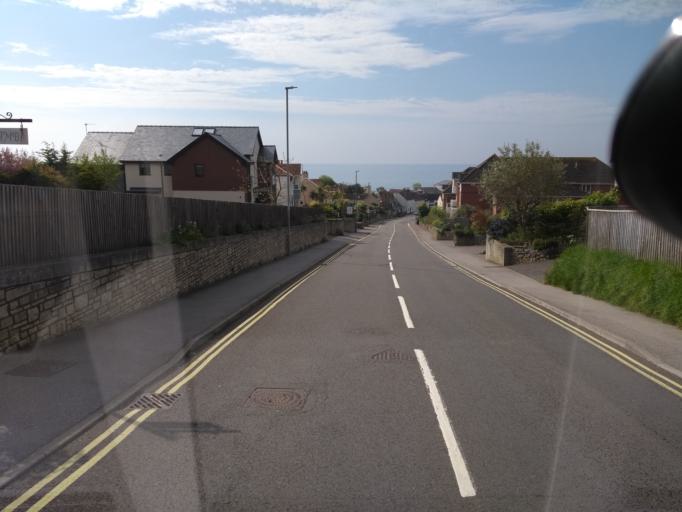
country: GB
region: England
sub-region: Dorset
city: Lyme Regis
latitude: 50.7286
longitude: -2.9316
